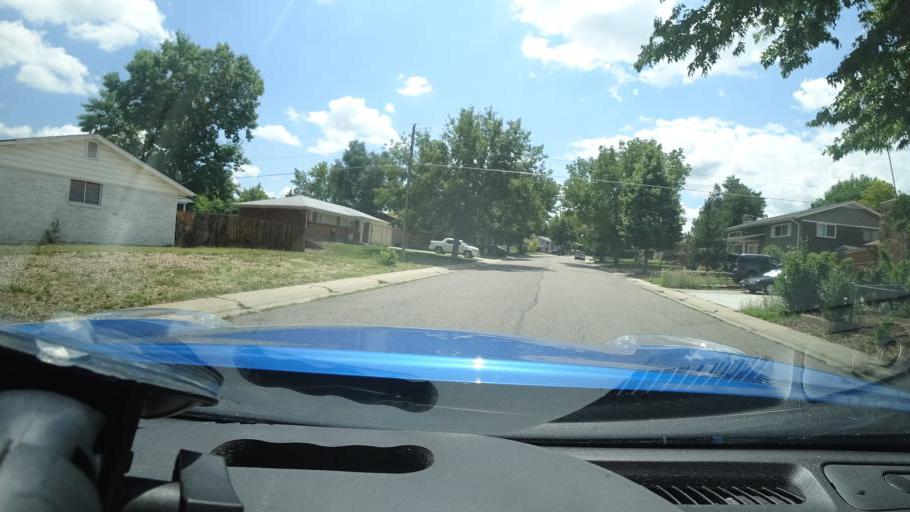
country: US
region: Colorado
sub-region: Adams County
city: Aurora
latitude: 39.7105
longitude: -104.8379
